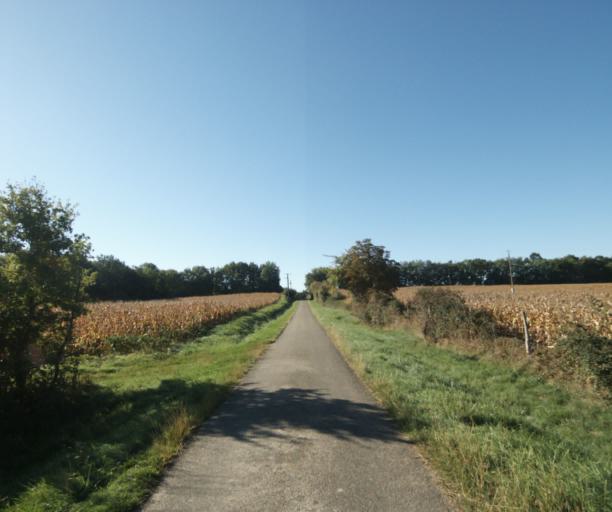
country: FR
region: Midi-Pyrenees
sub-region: Departement du Gers
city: Gondrin
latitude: 43.8138
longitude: 0.2325
